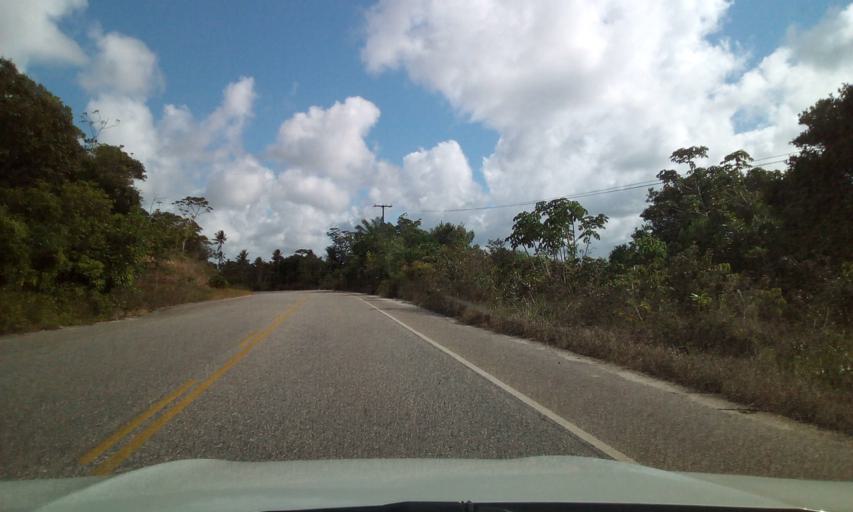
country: BR
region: Sergipe
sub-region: Estancia
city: Estancia
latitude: -11.3812
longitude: -37.4641
